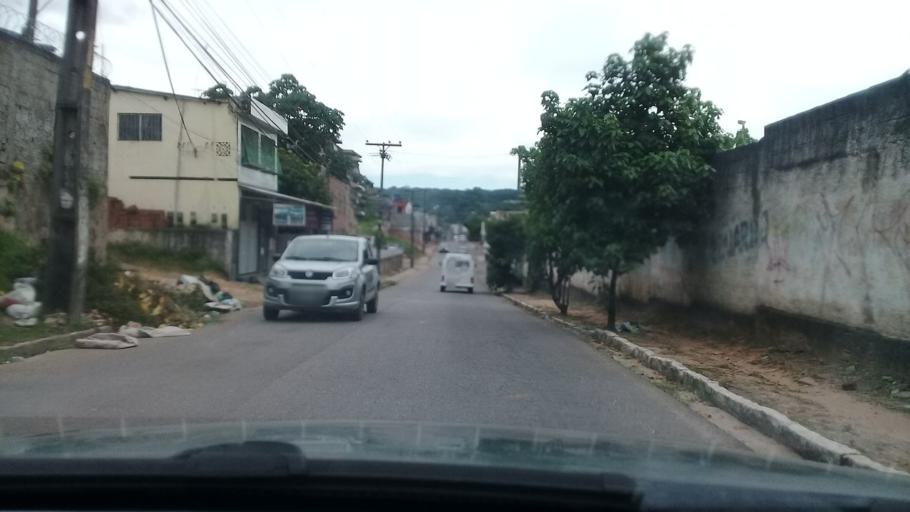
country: BR
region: Pernambuco
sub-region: Sao Lourenco Da Mata
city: Sao Lourenco da Mata
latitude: -8.0337
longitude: -34.9605
